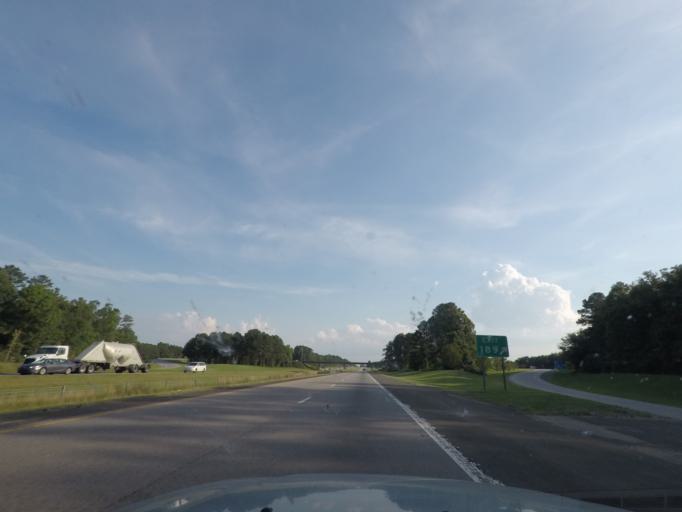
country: US
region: North Carolina
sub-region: Granville County
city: Butner
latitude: 36.1232
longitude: -78.7447
